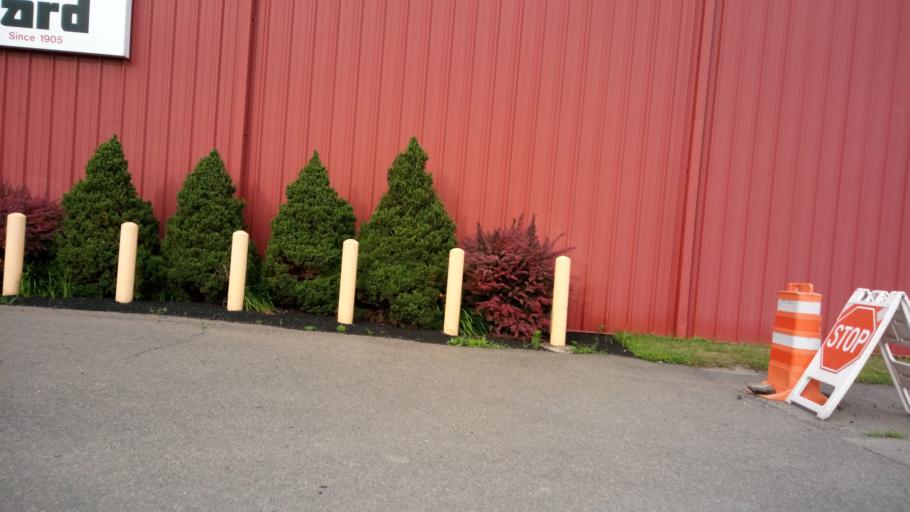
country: US
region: New York
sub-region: Chemung County
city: Elmira
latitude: 42.0941
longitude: -76.8094
